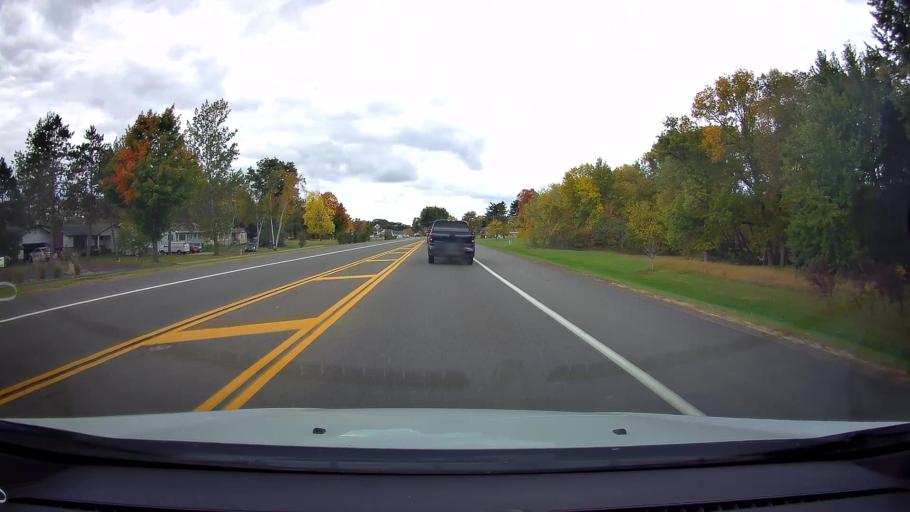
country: US
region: Minnesota
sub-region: Chisago County
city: Lindstrom
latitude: 45.3914
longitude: -92.8605
